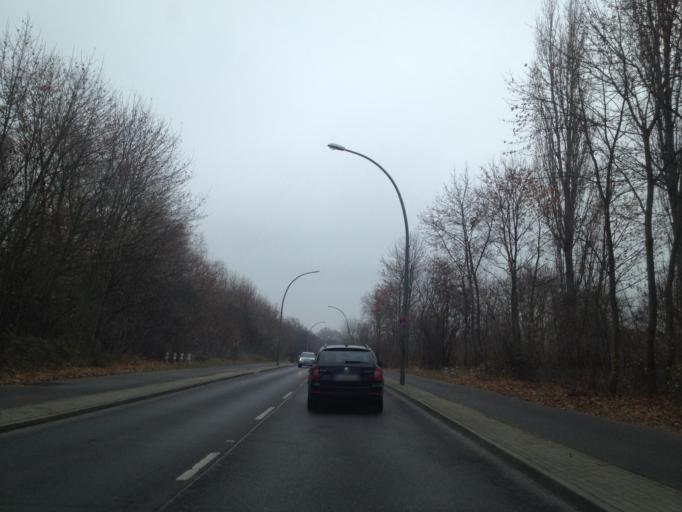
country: DE
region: Berlin
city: Blankenfelde
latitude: 52.6222
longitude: 13.3871
